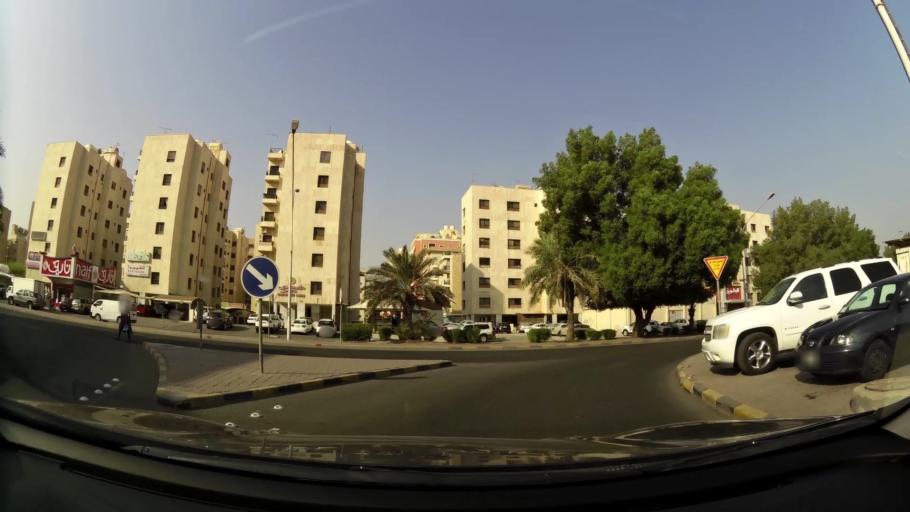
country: KW
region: Muhafazat Hawalli
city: Hawalli
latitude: 29.3237
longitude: 48.0314
